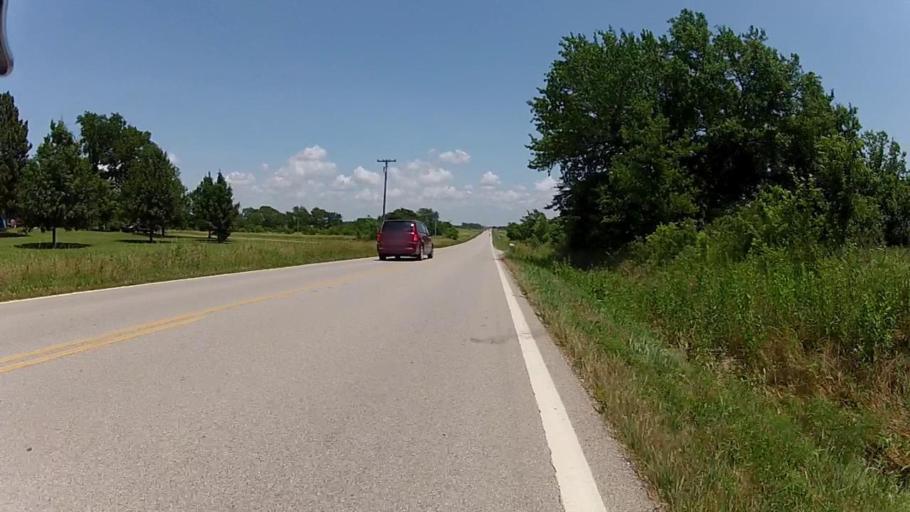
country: US
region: Kansas
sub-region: Montgomery County
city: Cherryvale
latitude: 37.1928
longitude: -95.4676
